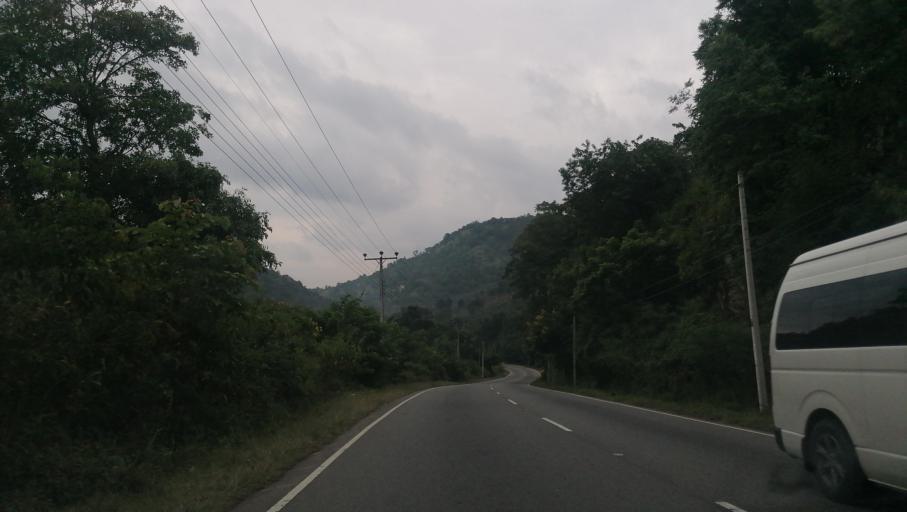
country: LK
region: Central
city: Kandy
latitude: 7.2460
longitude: 80.7271
